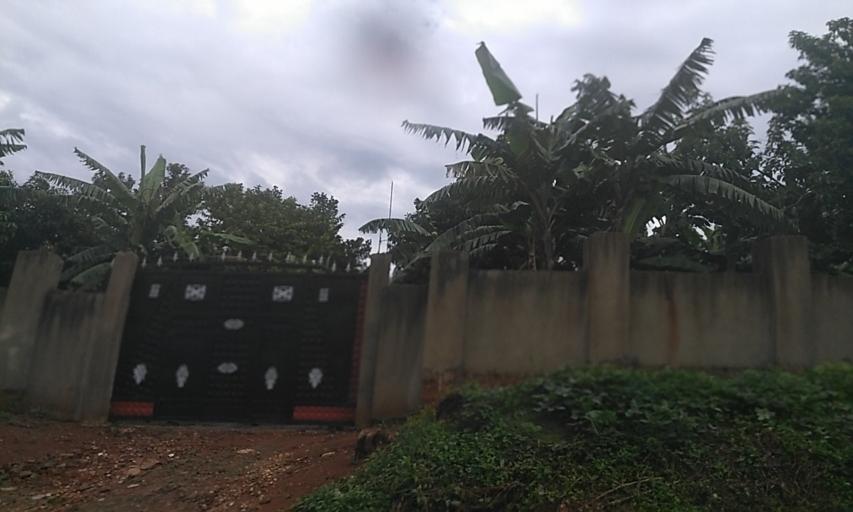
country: UG
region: Central Region
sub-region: Wakiso District
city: Bweyogerere
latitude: 0.3947
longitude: 32.6915
